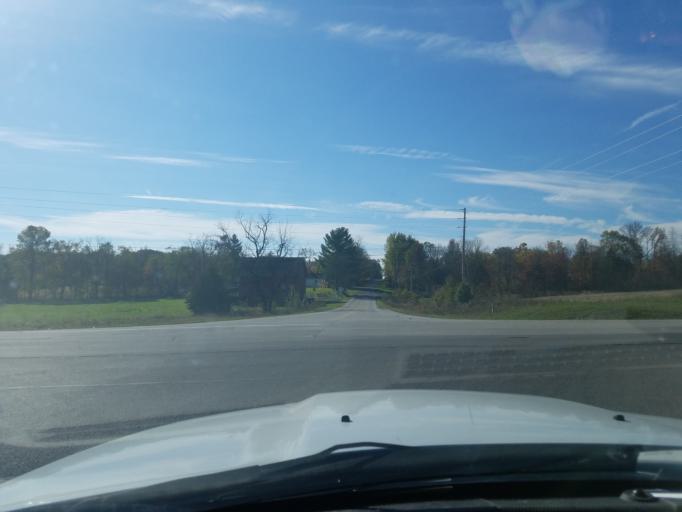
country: US
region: Indiana
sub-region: Jennings County
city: North Vernon
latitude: 39.0110
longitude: -85.5956
